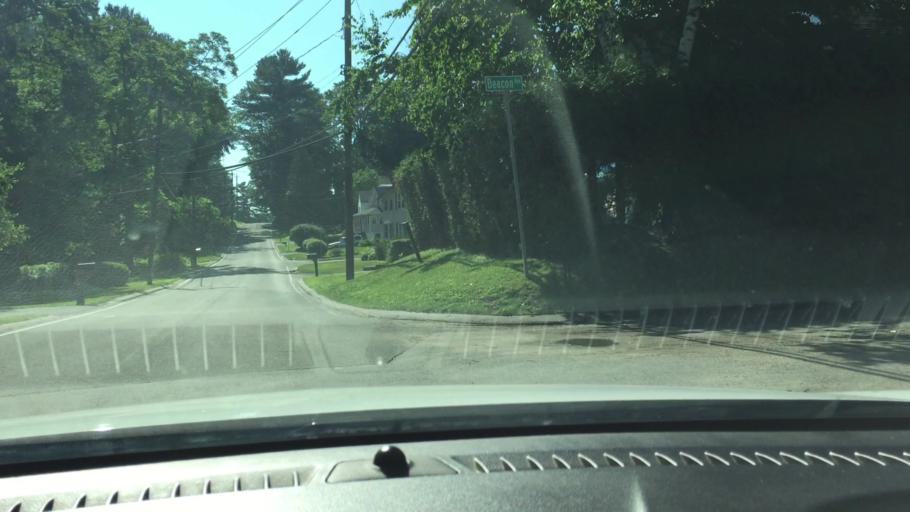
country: US
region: Massachusetts
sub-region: Berkshire County
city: Pittsfield
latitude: 42.4864
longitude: -73.2540
